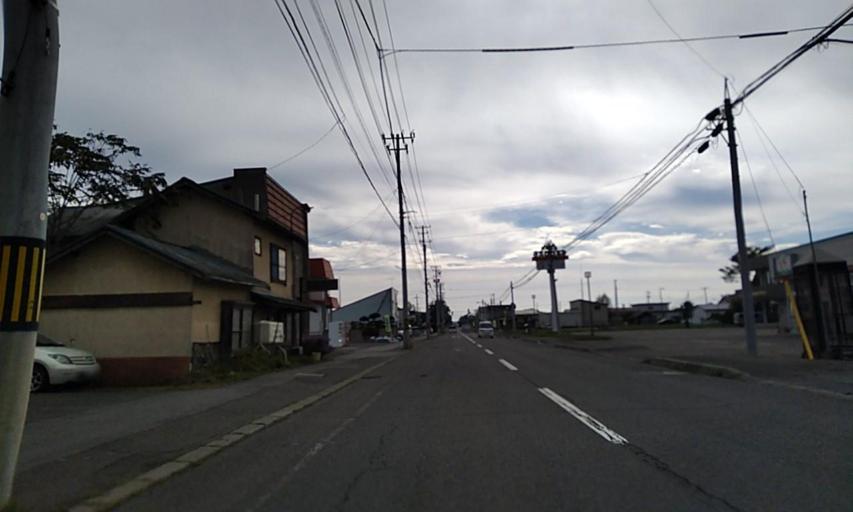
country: JP
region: Hokkaido
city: Obihiro
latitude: 42.8496
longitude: 143.1655
